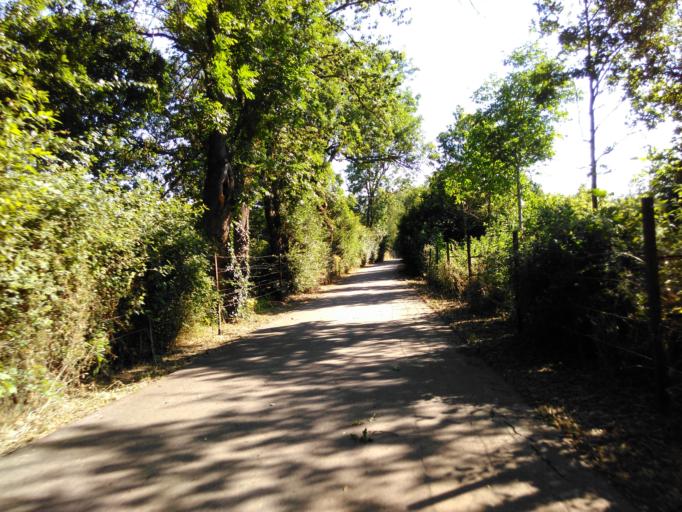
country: LU
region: Luxembourg
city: Belvaux
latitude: 49.5258
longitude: 5.9273
